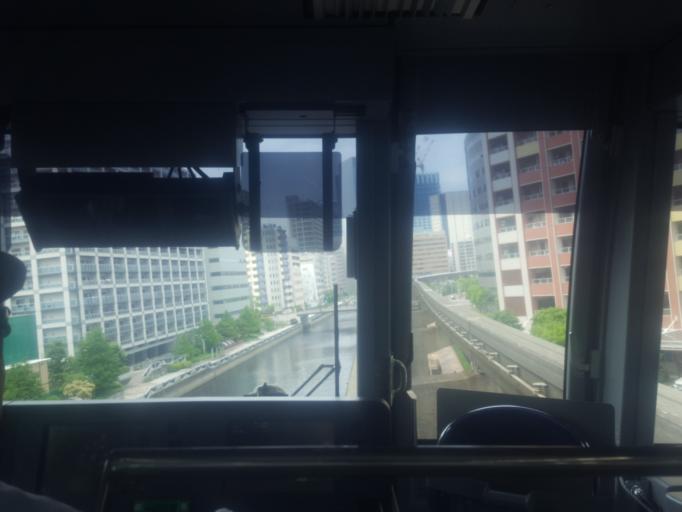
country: JP
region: Tokyo
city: Tokyo
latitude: 35.6367
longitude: 139.7497
